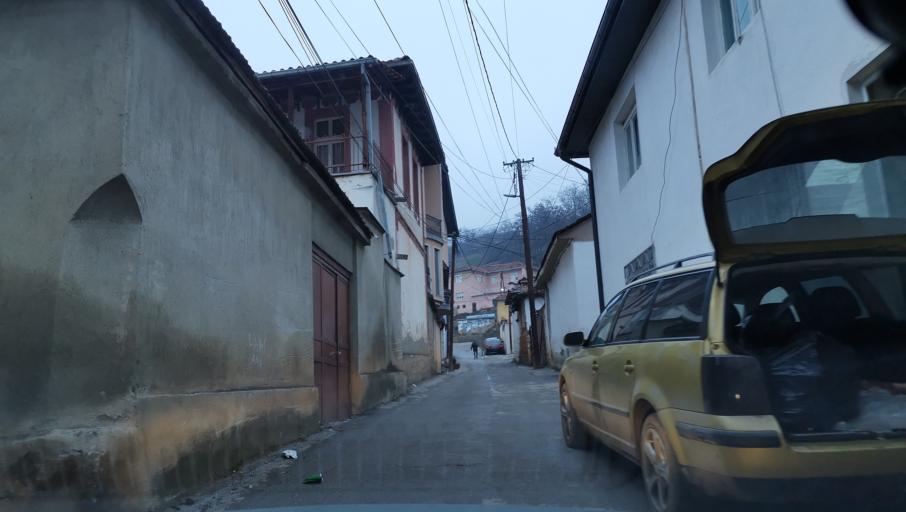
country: MK
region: Debar
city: Debar
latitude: 41.5242
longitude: 20.5275
